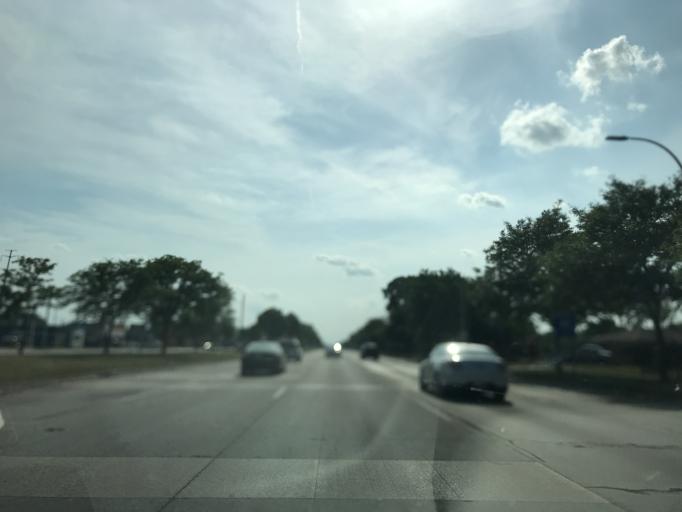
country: US
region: Michigan
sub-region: Wayne County
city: Wayne
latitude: 42.2855
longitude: -83.3493
